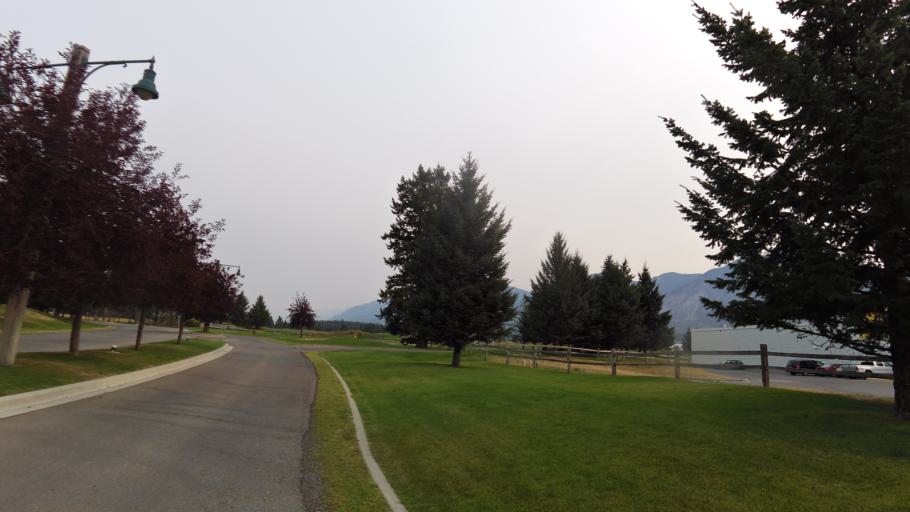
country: CA
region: British Columbia
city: Invermere
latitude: 50.5165
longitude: -116.0092
